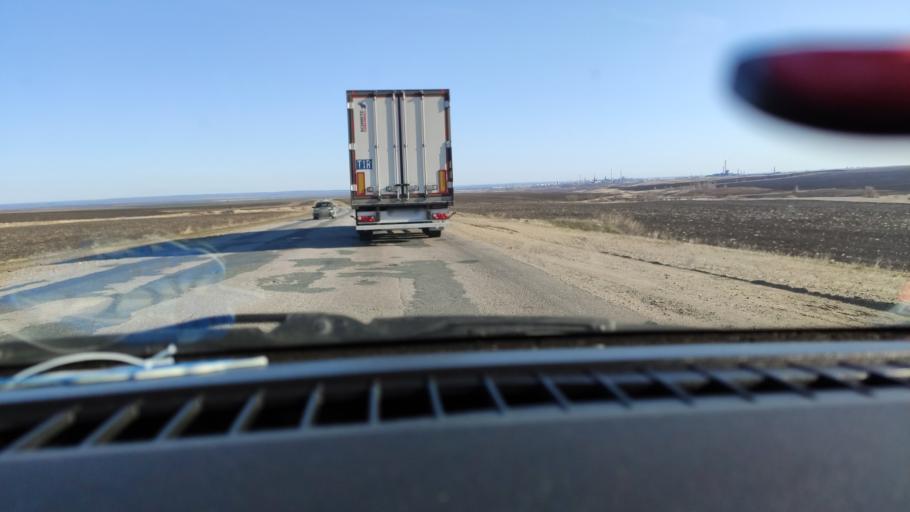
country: RU
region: Samara
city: Syzran'
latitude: 53.0065
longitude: 48.3320
